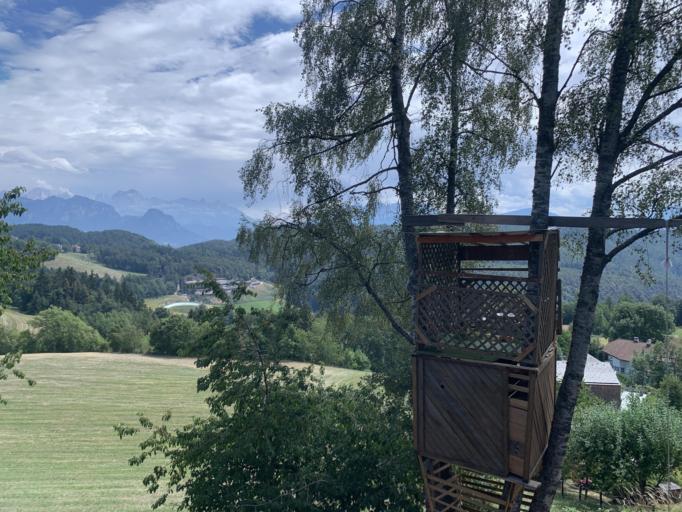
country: IT
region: Trentino-Alto Adige
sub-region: Bolzano
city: Soprabolzano
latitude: 46.5289
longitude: 11.4087
